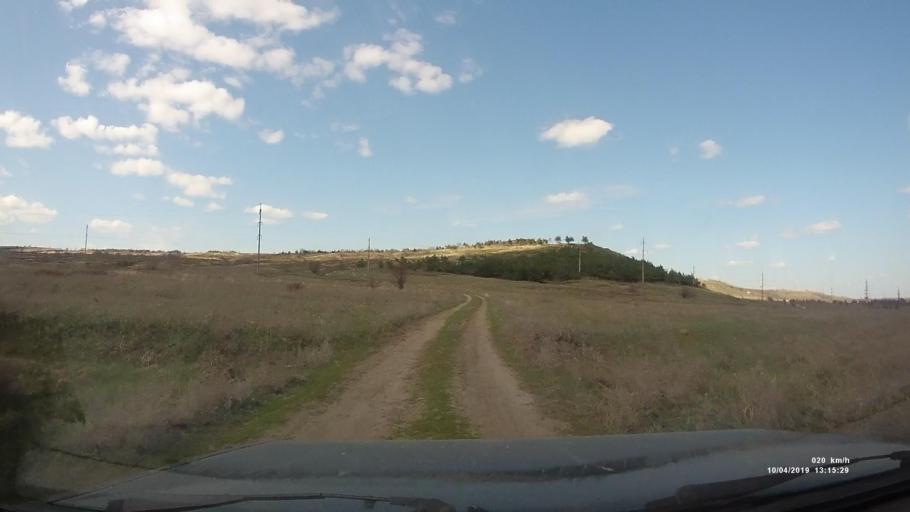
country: RU
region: Rostov
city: Masalovka
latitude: 48.4174
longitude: 40.2588
